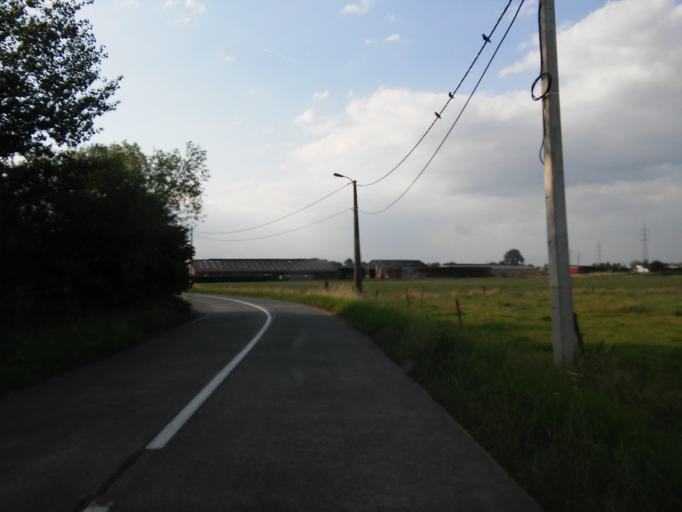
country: BE
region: Flanders
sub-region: Provincie Antwerpen
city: Rumst
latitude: 51.0899
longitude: 4.4627
